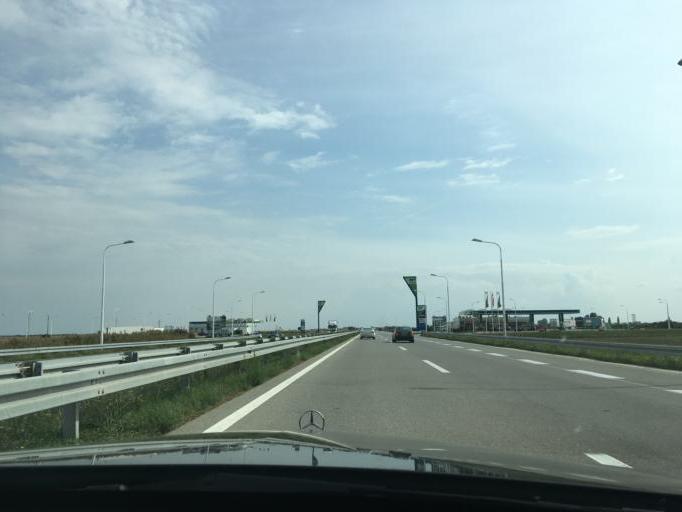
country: RS
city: Ravnje
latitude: 45.0368
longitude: 19.4470
